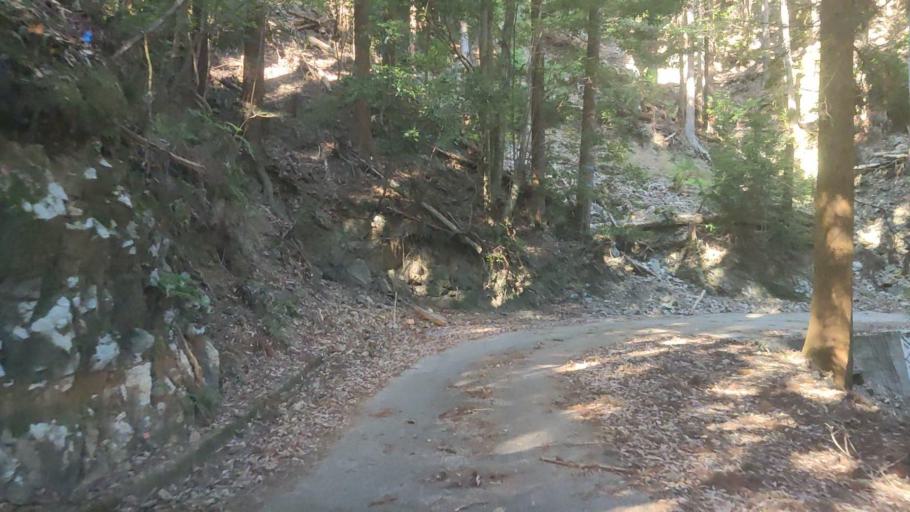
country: JP
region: Oita
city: Saiki
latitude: 32.7858
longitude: 131.8518
